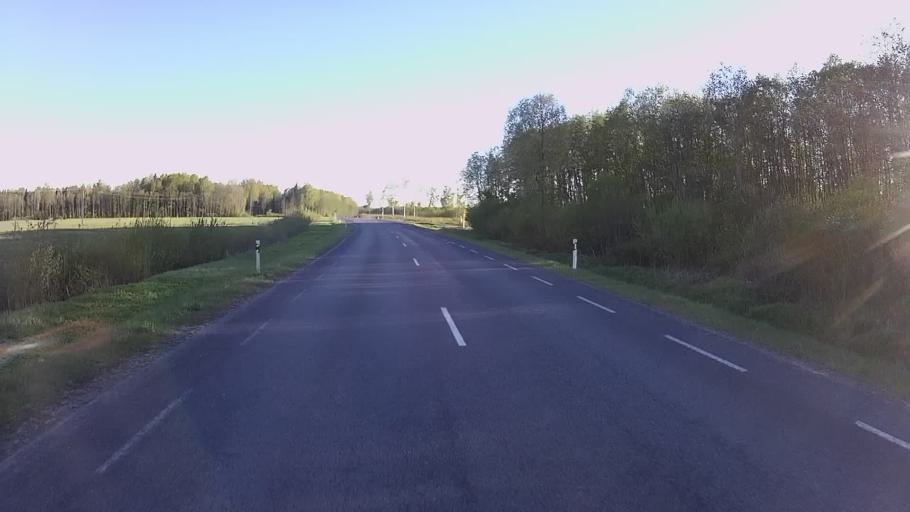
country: EE
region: Viljandimaa
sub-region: Viiratsi vald
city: Viiratsi
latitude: 58.4556
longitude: 25.7455
